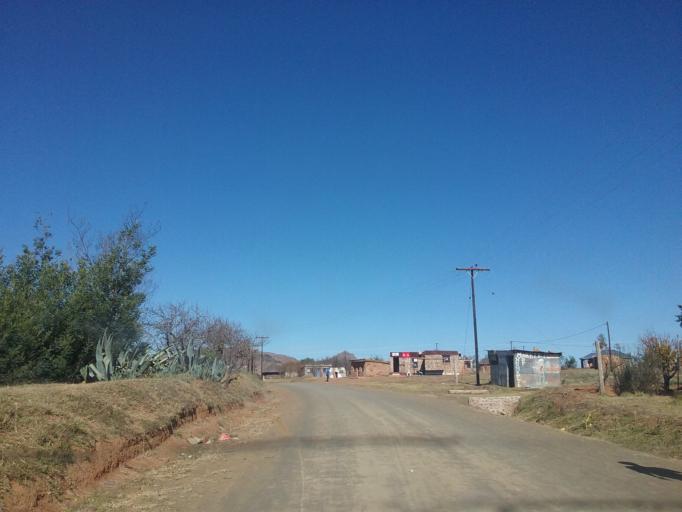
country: LS
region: Maseru
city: Maseru
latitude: -29.4518
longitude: 27.5780
